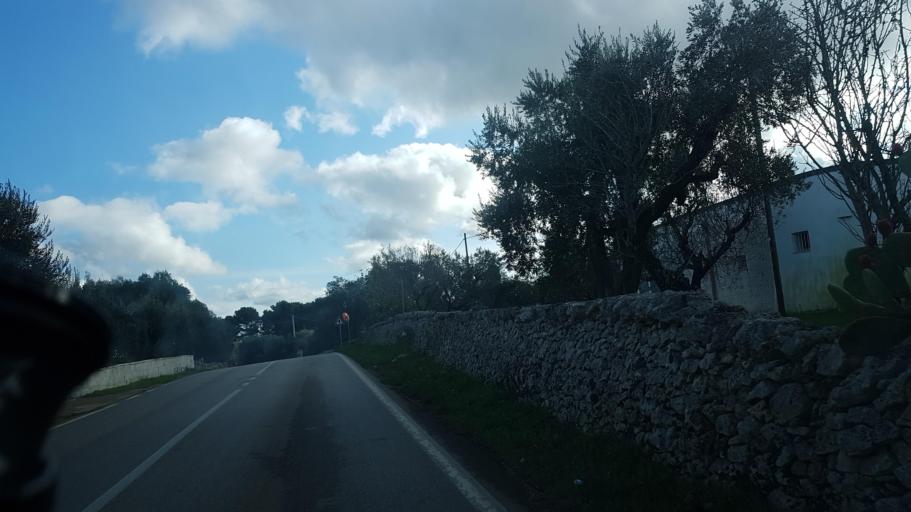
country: IT
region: Apulia
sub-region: Provincia di Brindisi
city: Ostuni
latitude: 40.6750
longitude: 17.5939
